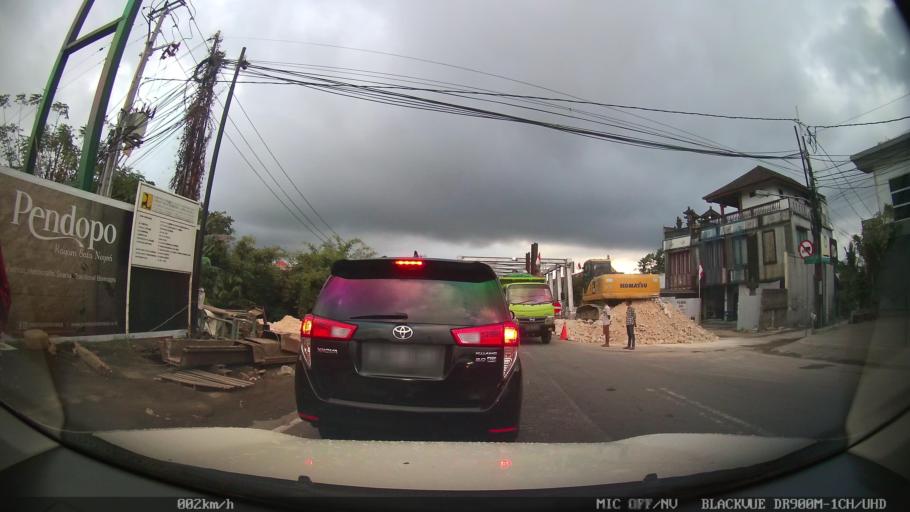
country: ID
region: Bali
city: Dajan Tangluk
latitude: -8.6357
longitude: 115.2321
